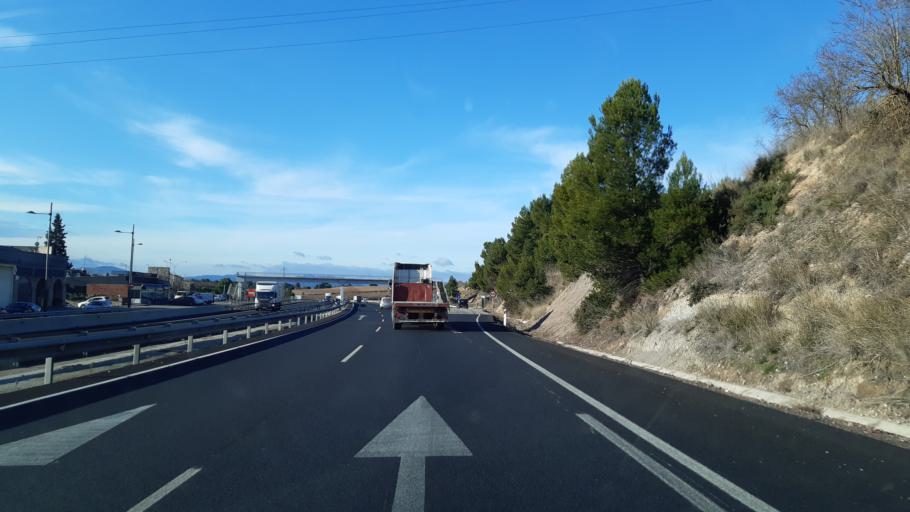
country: ES
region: Catalonia
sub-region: Provincia de Barcelona
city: Castelloli
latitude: 41.6000
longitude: 1.7023
